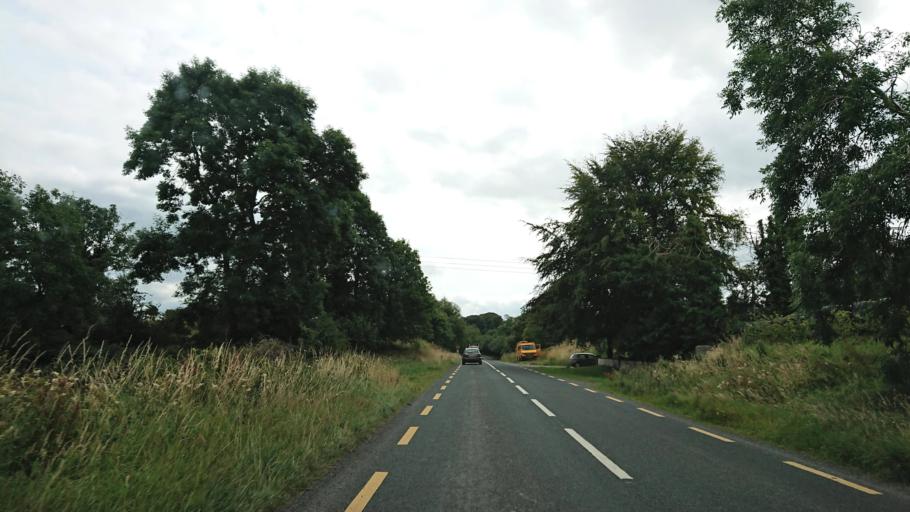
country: IE
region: Connaught
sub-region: County Leitrim
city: Carrick-on-Shannon
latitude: 54.0497
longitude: -8.0617
